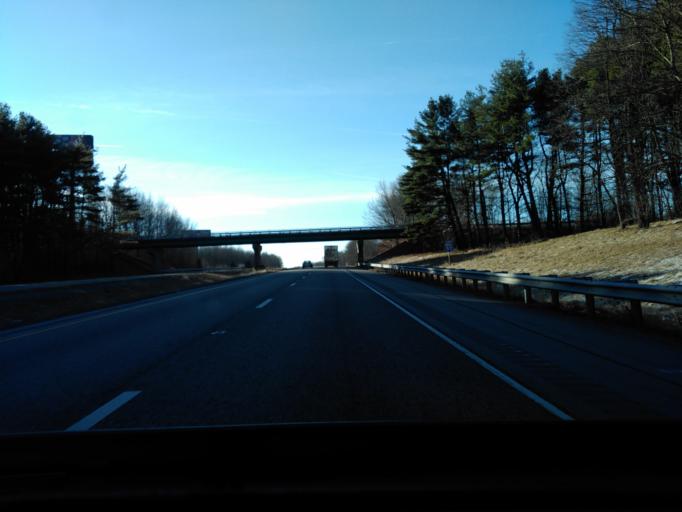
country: US
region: Illinois
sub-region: Franklin County
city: West Frankfort
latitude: 37.8926
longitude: -88.9455
